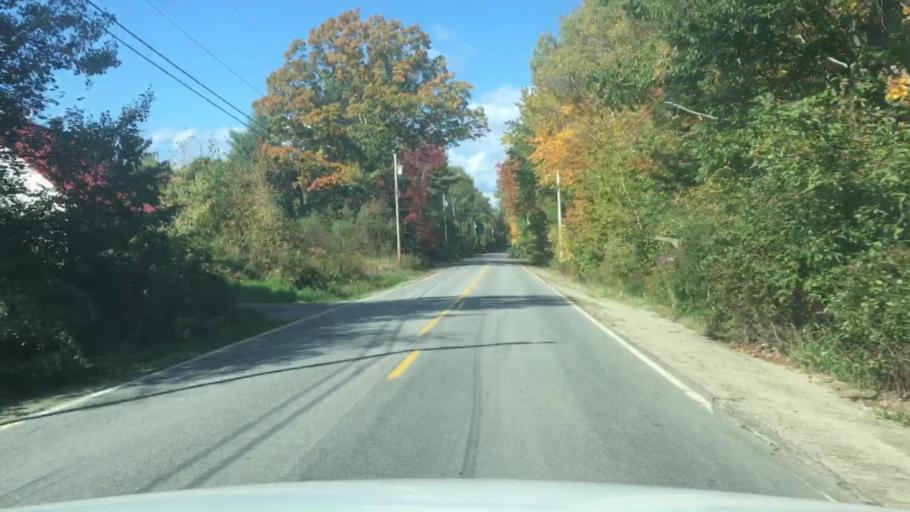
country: US
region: Maine
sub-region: Knox County
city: Warren
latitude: 44.0983
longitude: -69.2194
